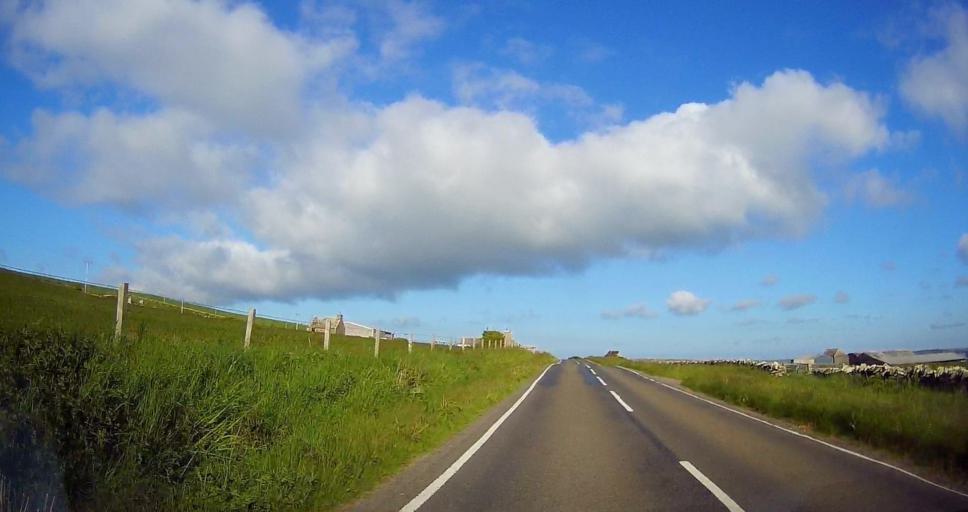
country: GB
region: Scotland
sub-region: Orkney Islands
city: Orkney
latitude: 58.9796
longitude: -3.0269
